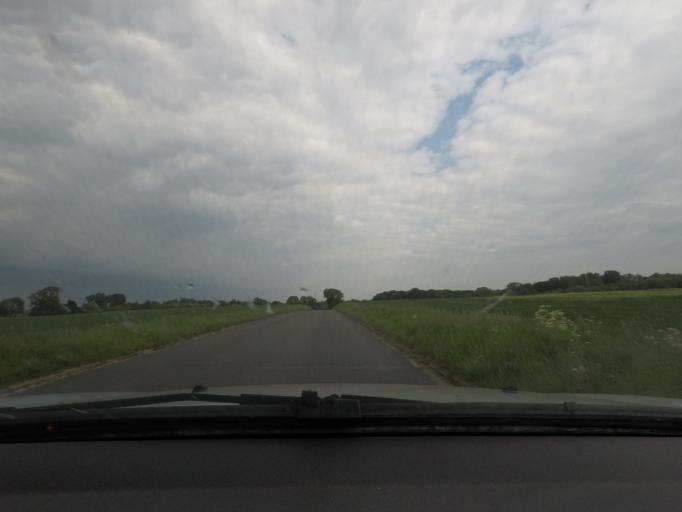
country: BE
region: Wallonia
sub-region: Province du Hainaut
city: Basse Lasne
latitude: 50.6613
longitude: 4.5015
